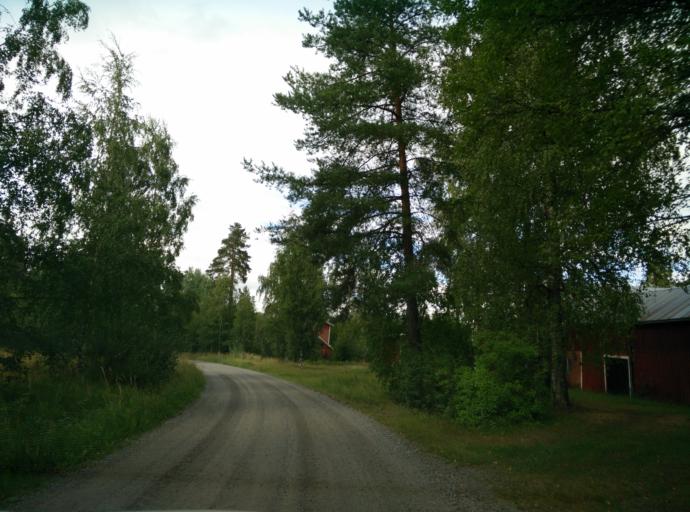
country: FI
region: Haeme
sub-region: Haemeenlinna
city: Kalvola
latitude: 61.1180
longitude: 24.1410
